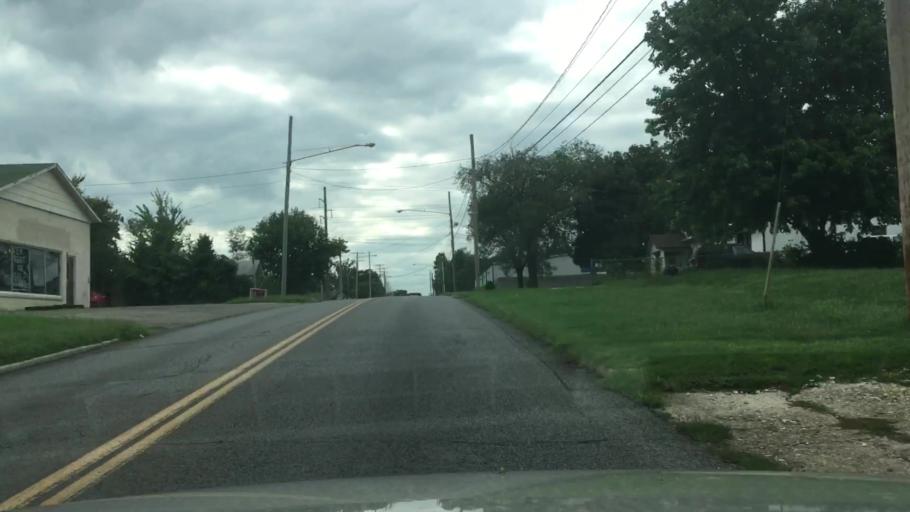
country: US
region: Oklahoma
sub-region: Cherokee County
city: Tahlequah
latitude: 35.9131
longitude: -94.9779
